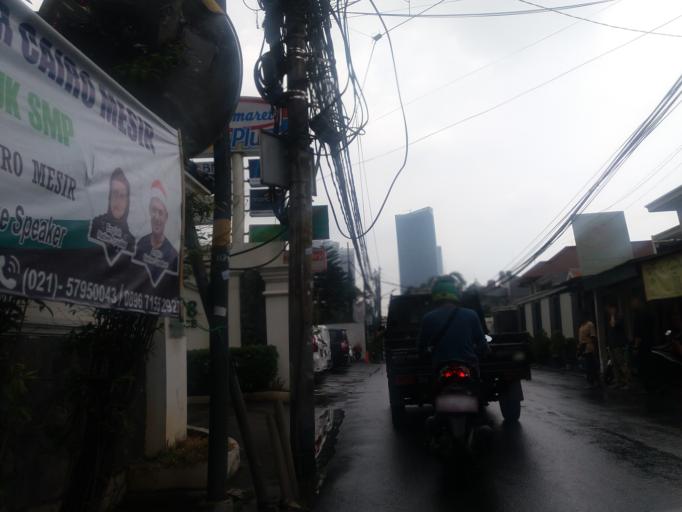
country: ID
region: Jakarta Raya
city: Jakarta
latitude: -6.2211
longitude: 106.8273
